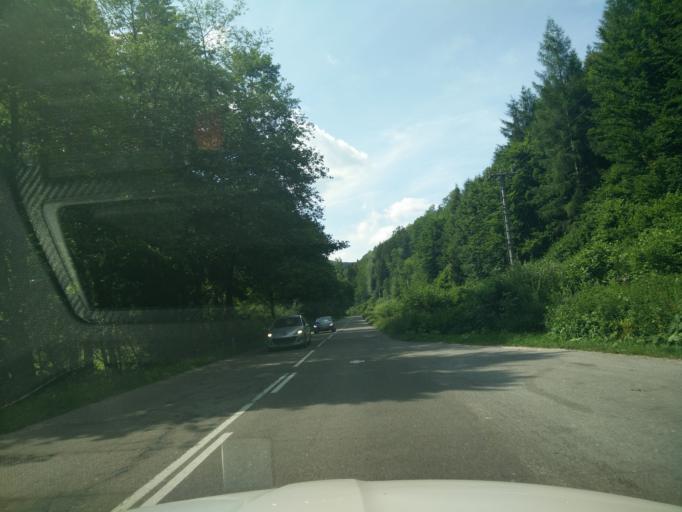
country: SK
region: Nitriansky
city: Bojnice
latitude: 48.9289
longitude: 18.6412
